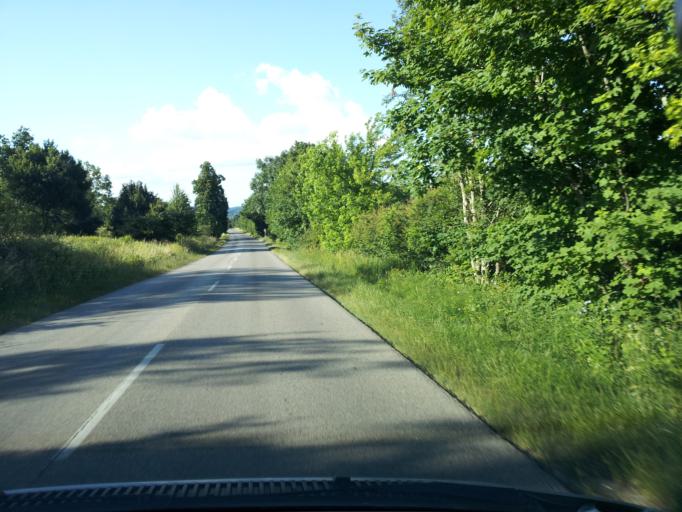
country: HU
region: Veszprem
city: Zirc
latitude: 47.2445
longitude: 17.8583
